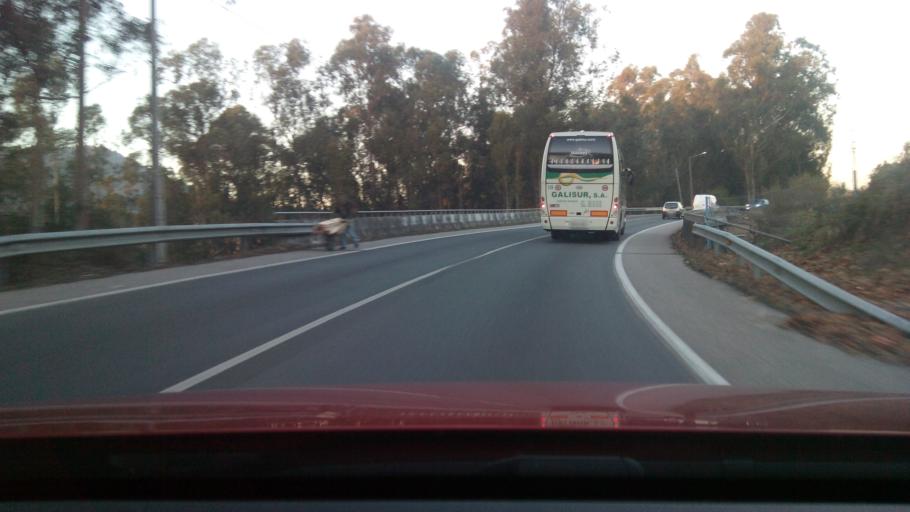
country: ES
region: Galicia
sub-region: Provincia de Pontevedra
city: Gondomar
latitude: 42.1515
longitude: -8.7264
